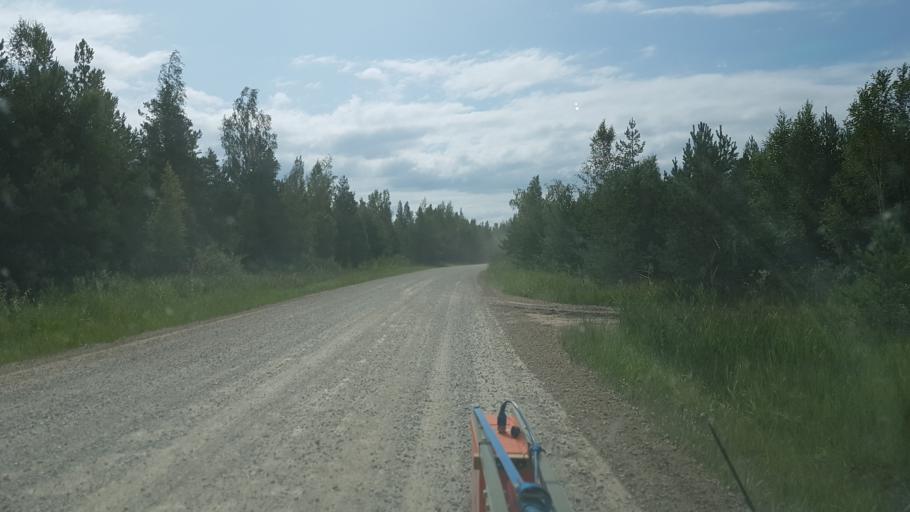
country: EE
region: Paernumaa
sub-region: Audru vald
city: Audru
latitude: 58.5272
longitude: 24.4071
